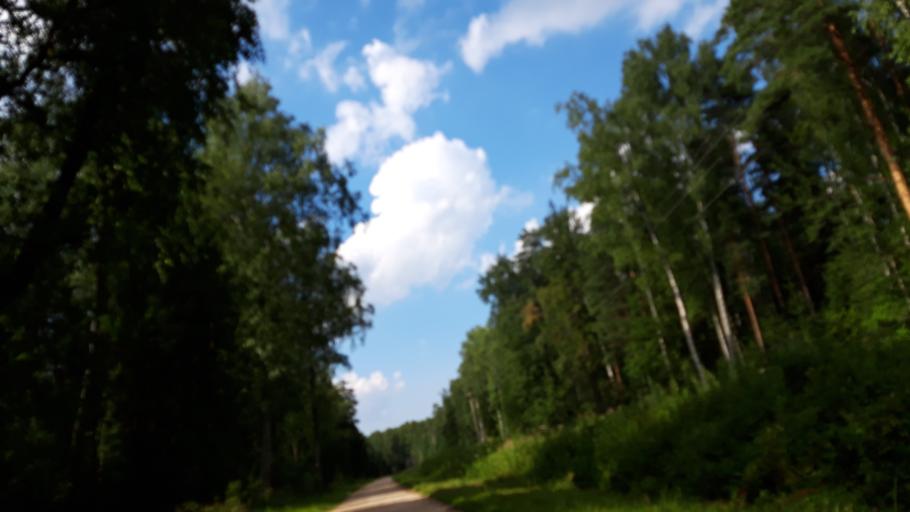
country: RU
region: Tverskaya
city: Konakovo
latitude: 56.6857
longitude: 36.7112
